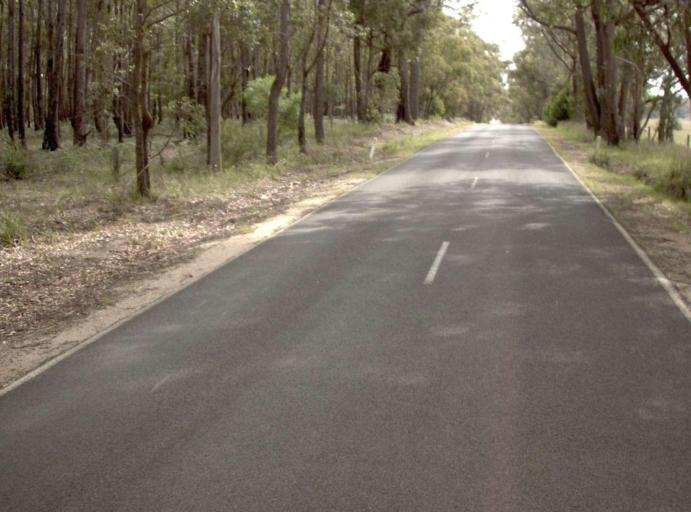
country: AU
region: Victoria
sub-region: Latrobe
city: Traralgon
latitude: -38.3796
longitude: 146.7721
